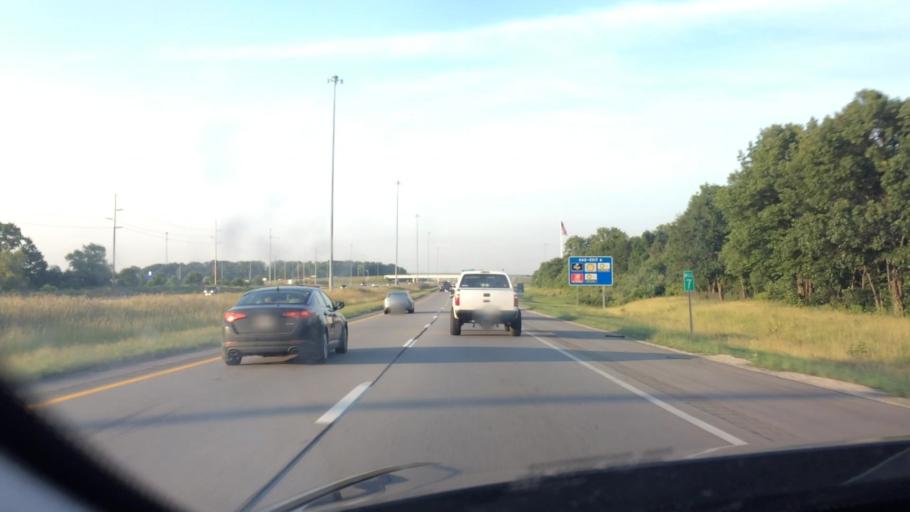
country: US
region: Ohio
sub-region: Lucas County
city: Holland
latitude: 41.5885
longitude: -83.6898
